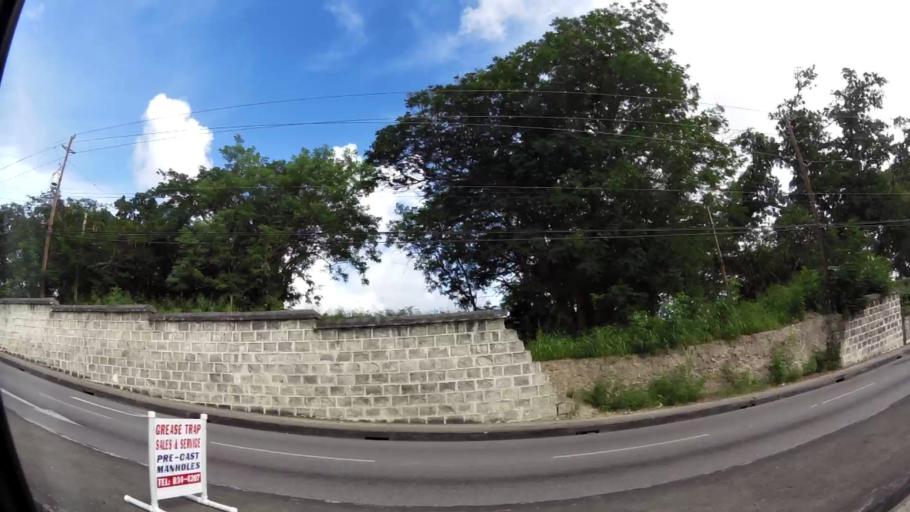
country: BB
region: Saint Michael
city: Bridgetown
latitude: 13.1261
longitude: -59.6068
